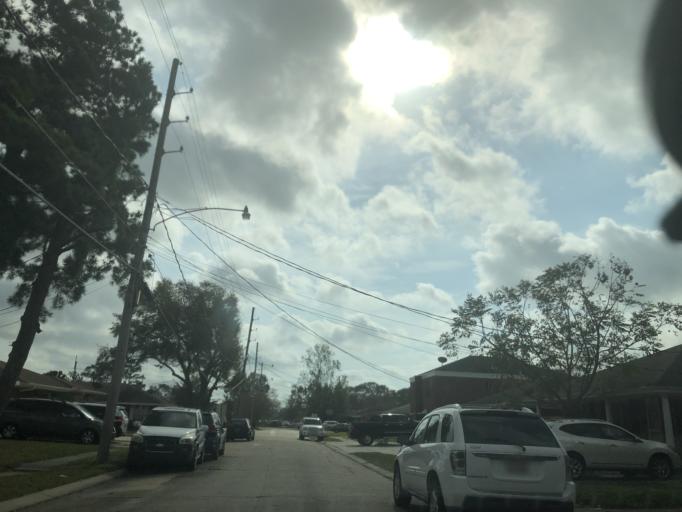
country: US
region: Louisiana
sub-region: Jefferson Parish
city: Metairie
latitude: 29.9939
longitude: -90.1576
